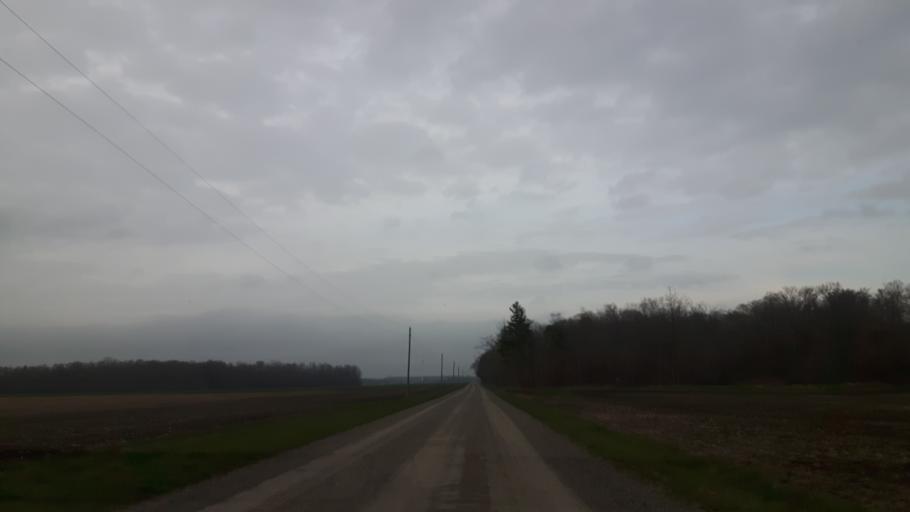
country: CA
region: Ontario
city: Bluewater
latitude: 43.5099
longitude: -81.6911
